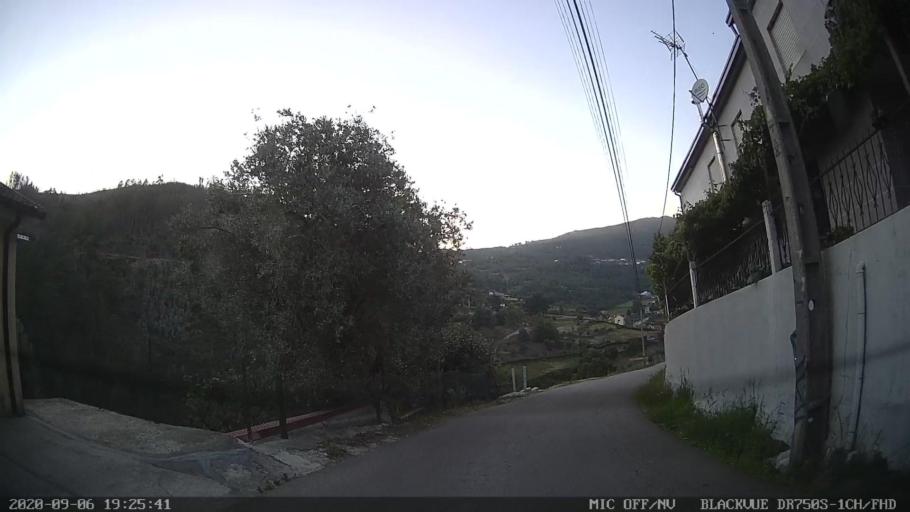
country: PT
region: Vila Real
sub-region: Mesao Frio
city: Mesao Frio
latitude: 41.1867
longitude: -7.9221
